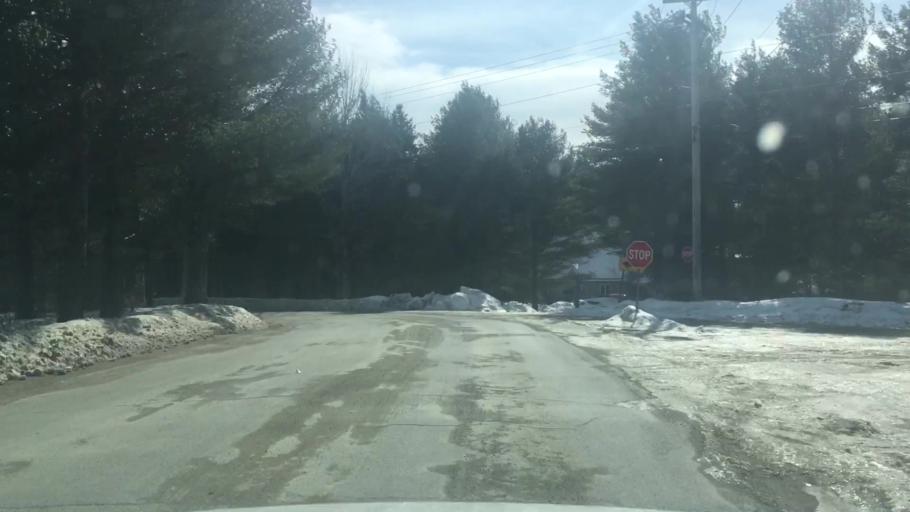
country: US
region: Maine
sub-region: Penobscot County
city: Holden
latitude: 44.7669
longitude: -68.6473
